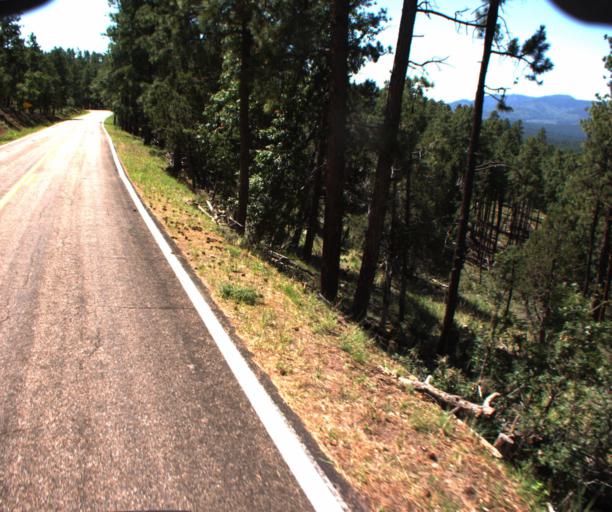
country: US
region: Arizona
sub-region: Greenlee County
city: Morenci
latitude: 33.5438
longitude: -109.3178
